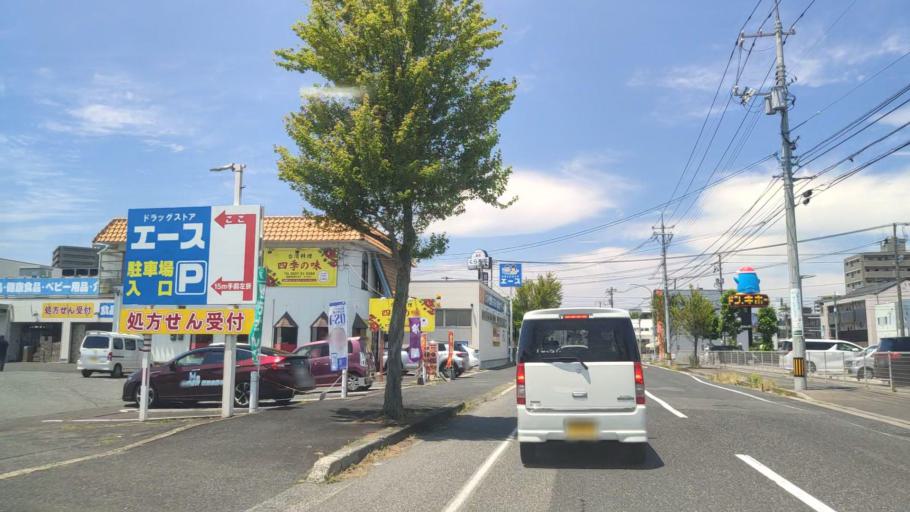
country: JP
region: Tottori
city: Tottori
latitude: 35.4877
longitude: 134.2326
